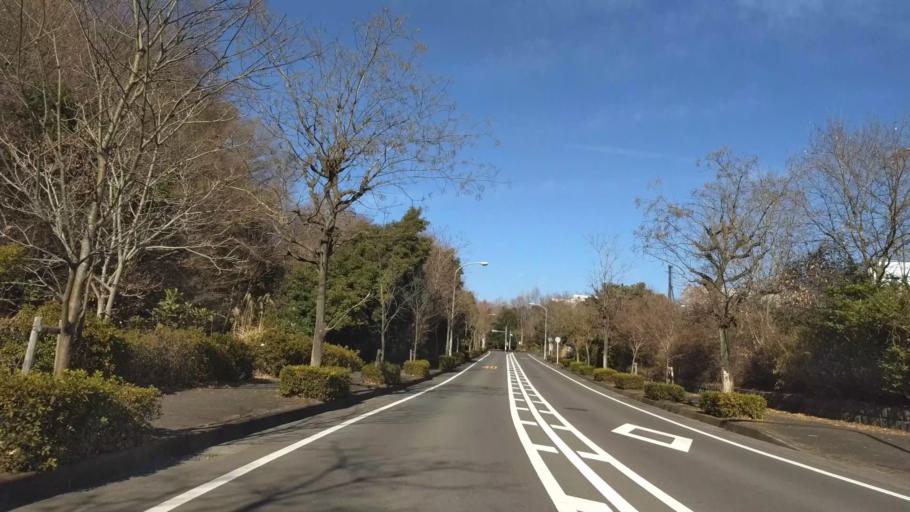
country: JP
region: Kanagawa
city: Hadano
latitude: 35.3428
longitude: 139.2218
